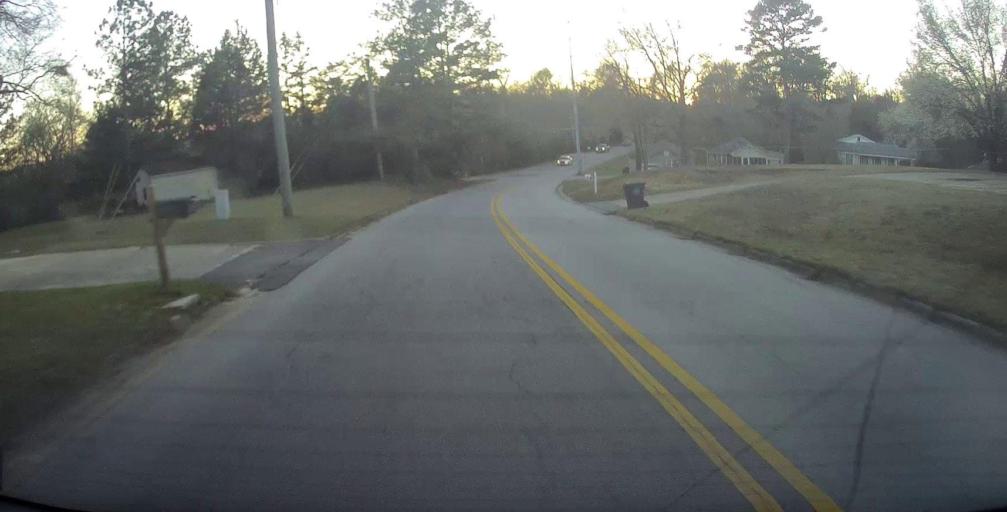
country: US
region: Alabama
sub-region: Russell County
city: Phenix City
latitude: 32.4856
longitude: -85.0224
